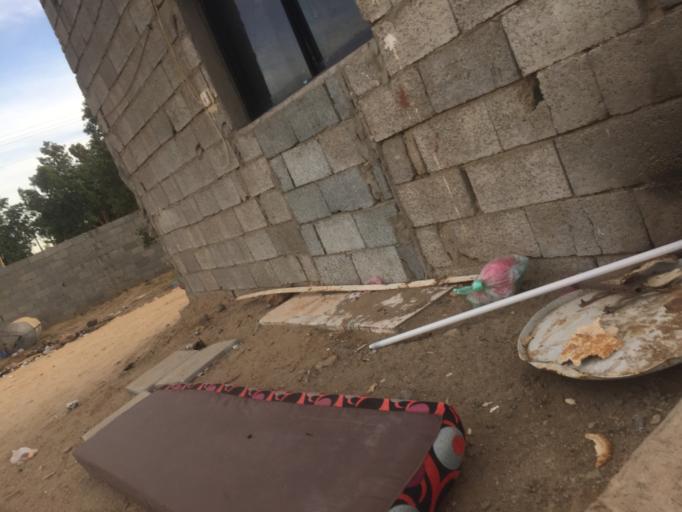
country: SA
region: Makkah
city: Al Jumum
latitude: 21.5148
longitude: 39.6178
